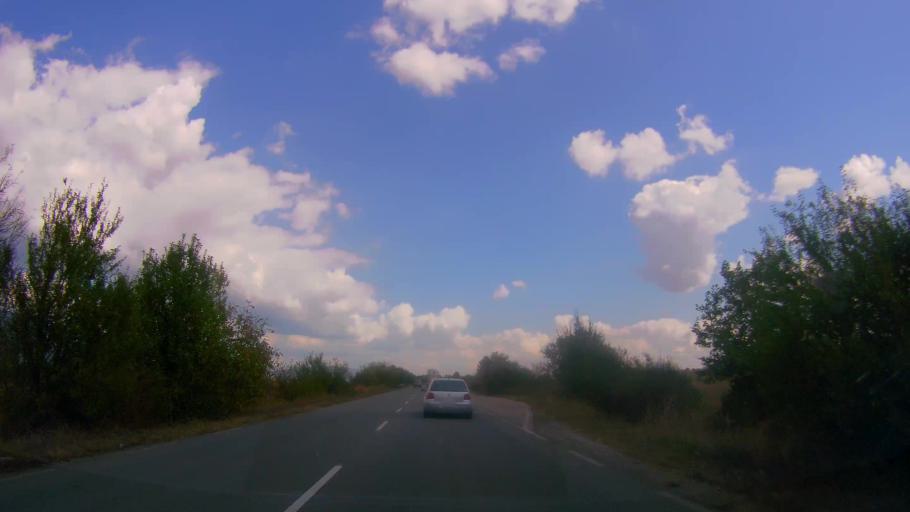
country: BG
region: Sliven
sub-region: Obshtina Tvurditsa
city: Tvurditsa
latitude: 42.6573
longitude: 25.9122
